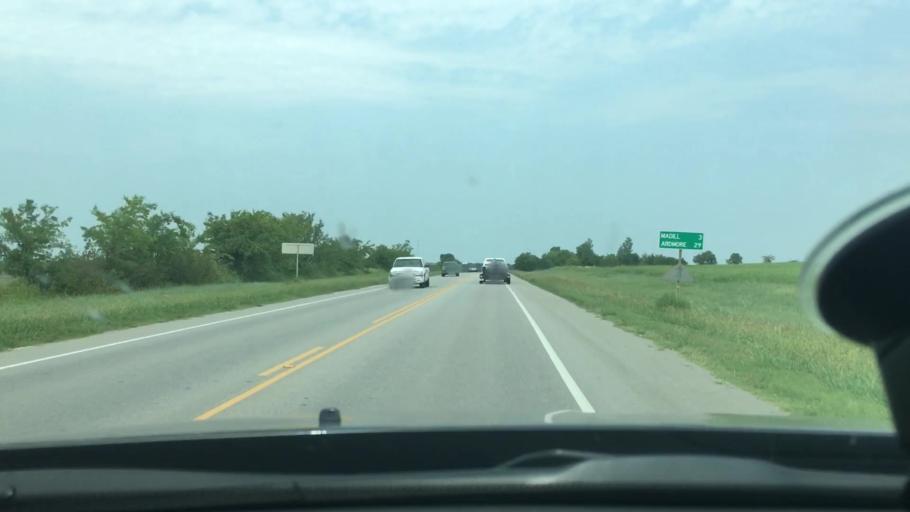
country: US
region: Oklahoma
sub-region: Marshall County
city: Madill
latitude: 34.0522
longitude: -96.7446
